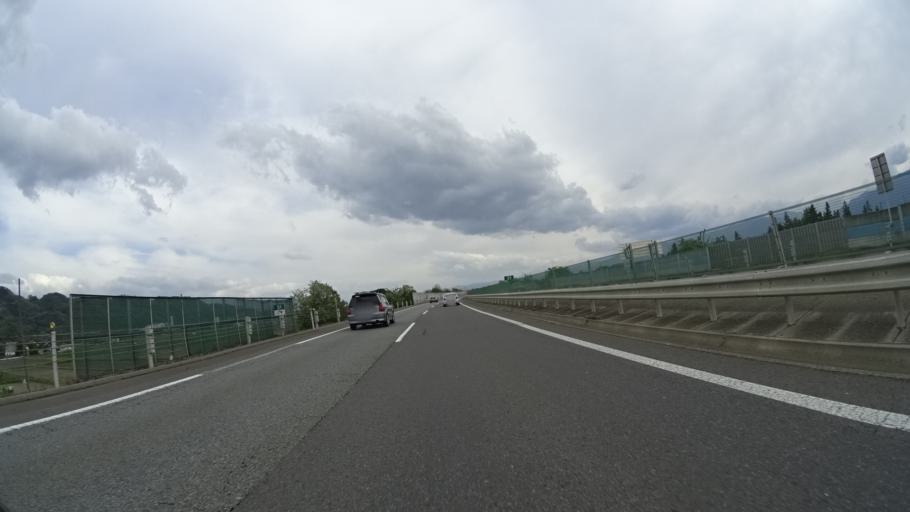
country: JP
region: Nagano
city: Toyoshina
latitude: 36.2811
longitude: 137.9312
